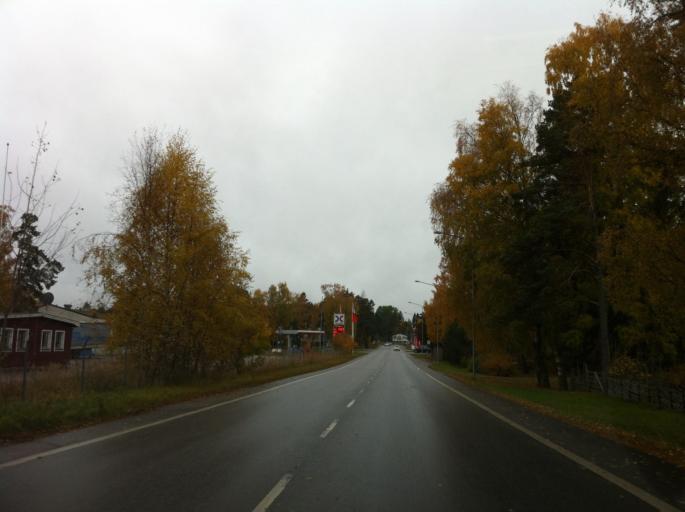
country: SE
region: Uppsala
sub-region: Osthammars Kommun
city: OEsthammar
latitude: 60.2571
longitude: 18.3517
